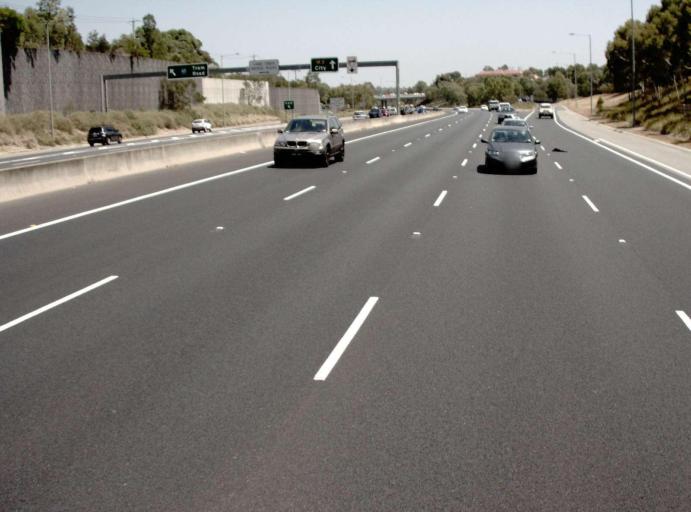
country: AU
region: Victoria
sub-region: Whitehorse
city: Box Hill North
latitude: -37.7973
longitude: 145.1329
